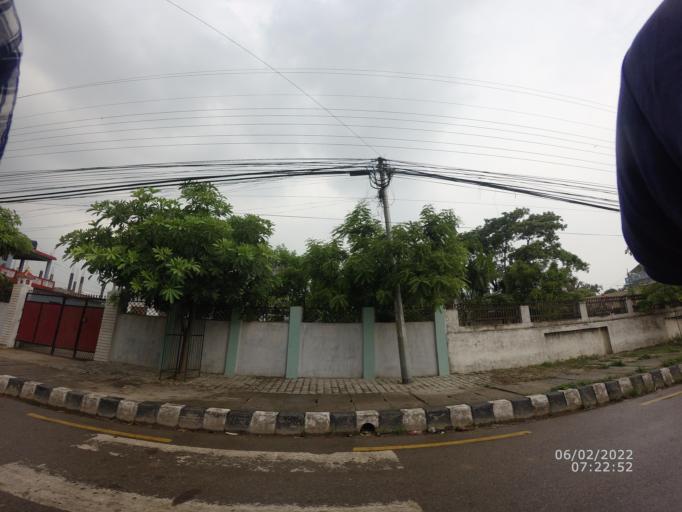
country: NP
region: Western Region
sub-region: Lumbini Zone
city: Bhairahawa
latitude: 27.4931
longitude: 83.4456
